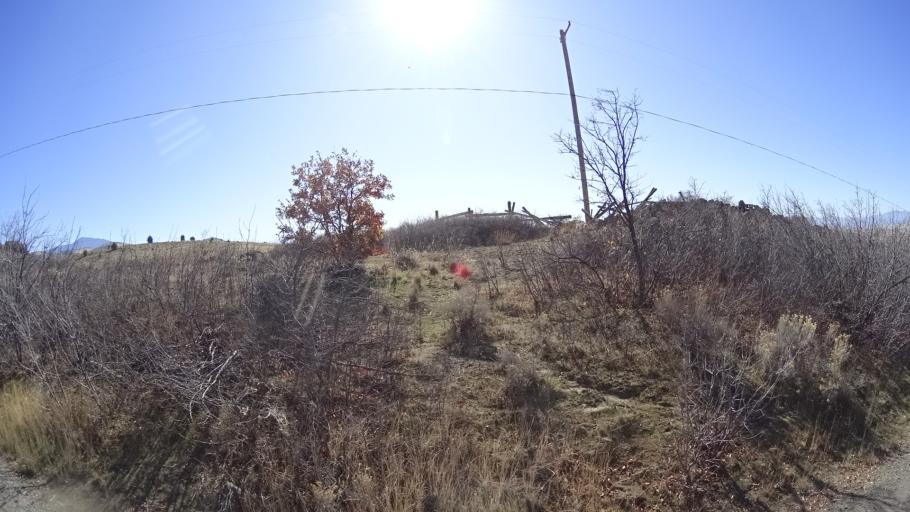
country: US
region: California
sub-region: Siskiyou County
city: Montague
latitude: 41.8323
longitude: -122.3829
